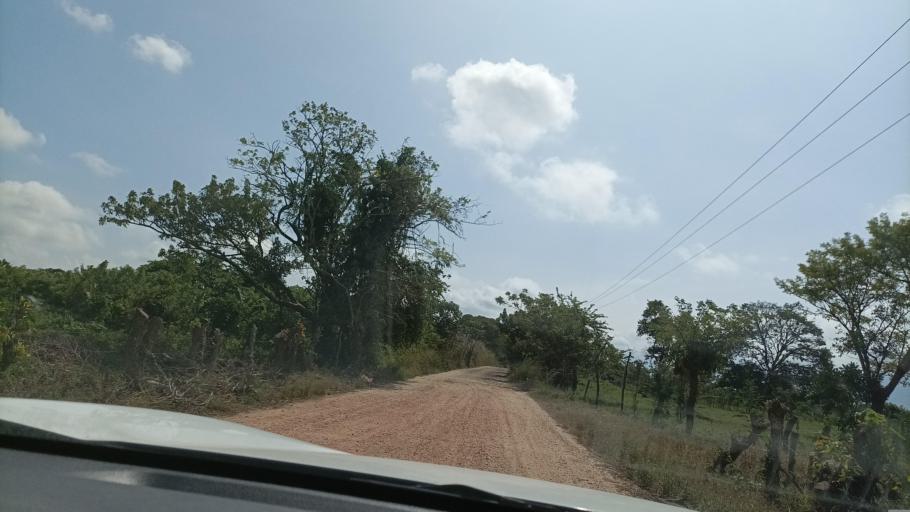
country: MX
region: Veracruz
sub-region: Chinameca
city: Chacalapa
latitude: 18.1334
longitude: -94.6553
